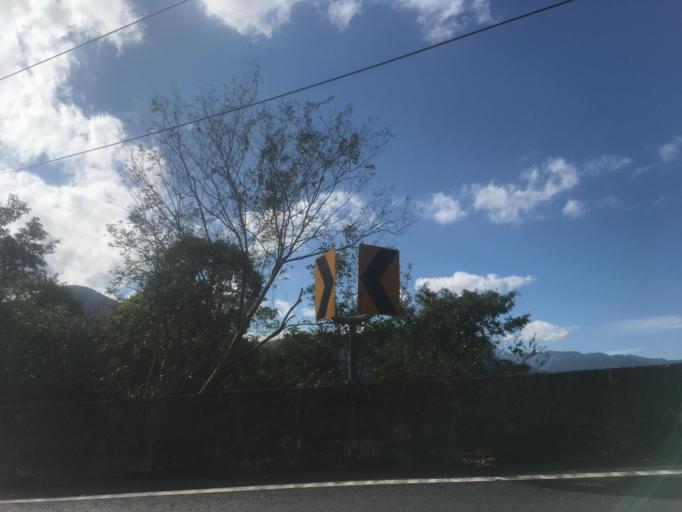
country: TW
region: Taiwan
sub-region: Yilan
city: Yilan
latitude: 24.6281
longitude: 121.5447
